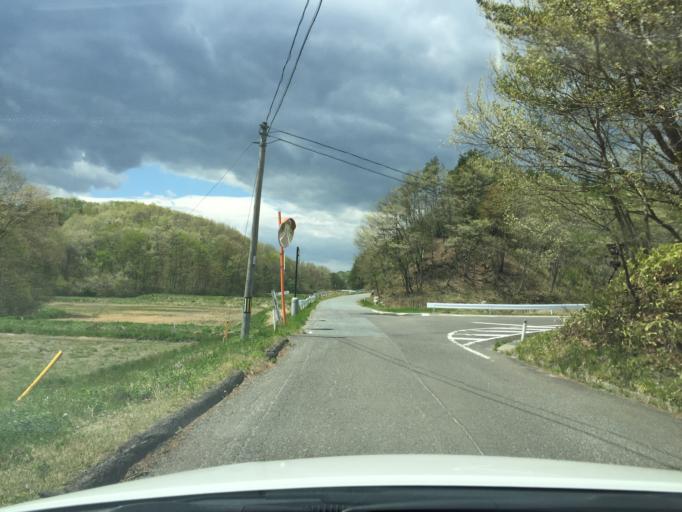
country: JP
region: Fukushima
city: Yanagawamachi-saiwaicho
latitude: 37.6972
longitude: 140.6708
